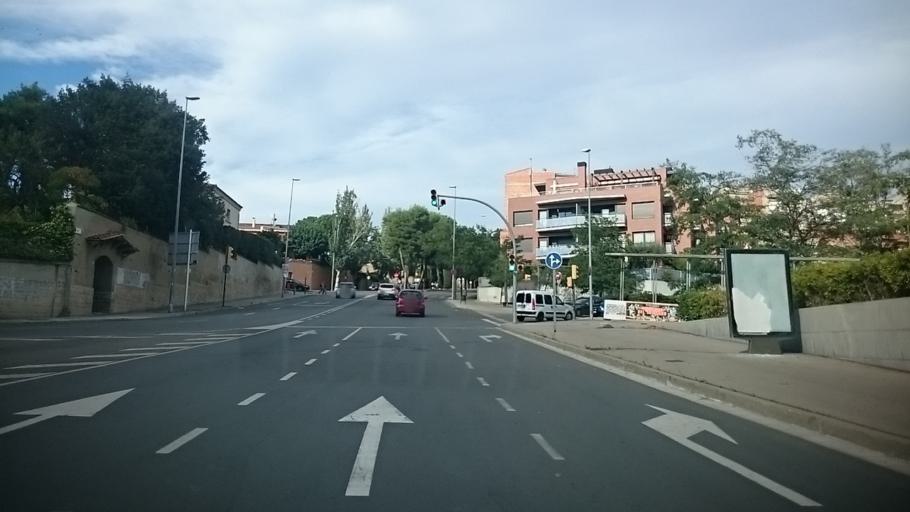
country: ES
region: Catalonia
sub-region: Provincia de Barcelona
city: Igualada
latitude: 41.5838
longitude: 1.6119
